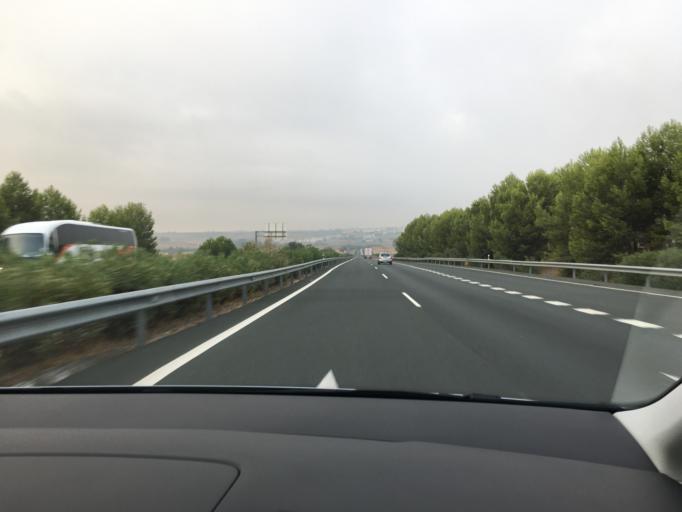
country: ES
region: Andalusia
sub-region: Province of Cordoba
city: La Carlota
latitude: 37.6951
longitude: -4.9197
